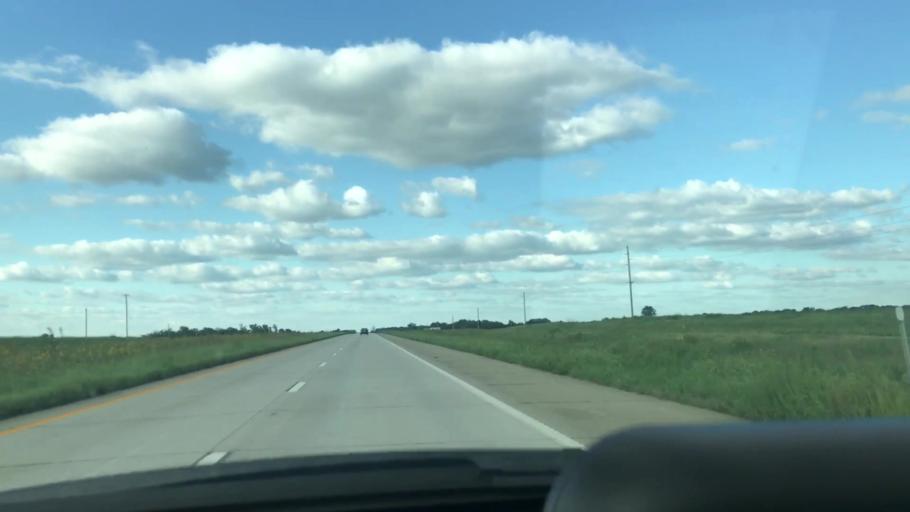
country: US
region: Missouri
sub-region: Benton County
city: Cole Camp
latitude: 38.5145
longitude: -93.2725
